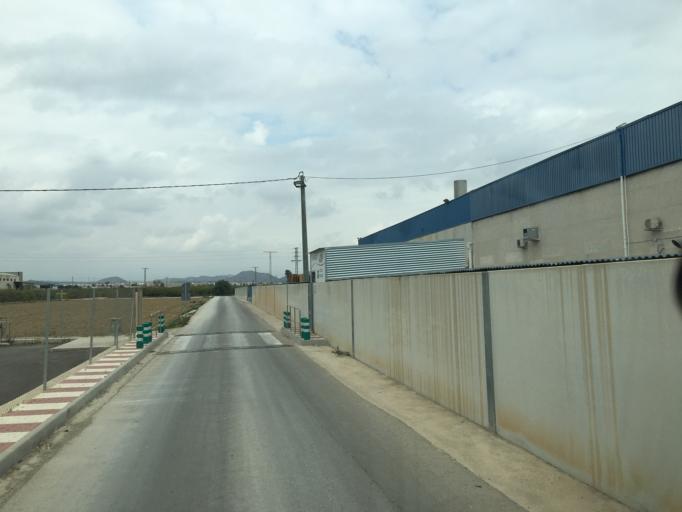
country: ES
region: Murcia
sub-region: Murcia
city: Santomera
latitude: 38.0445
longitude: -1.0323
